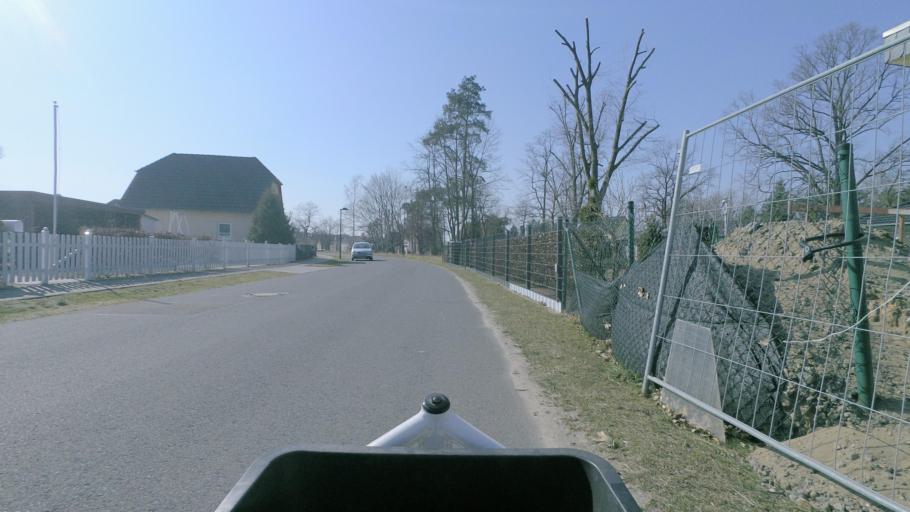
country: DE
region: Brandenburg
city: Sperenberg
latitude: 52.1661
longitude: 13.3715
